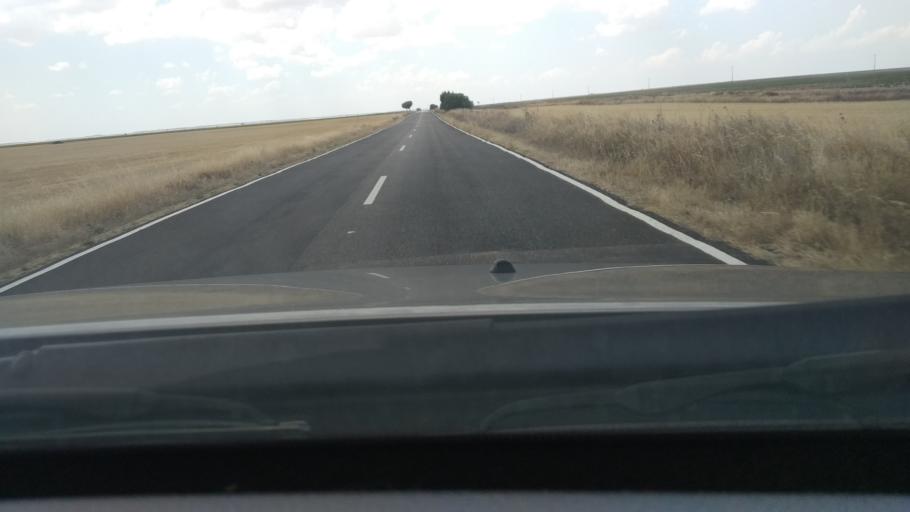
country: ES
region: Castille and Leon
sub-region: Provincia de Burgos
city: Iglesiarrubia
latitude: 41.9457
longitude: -3.8469
